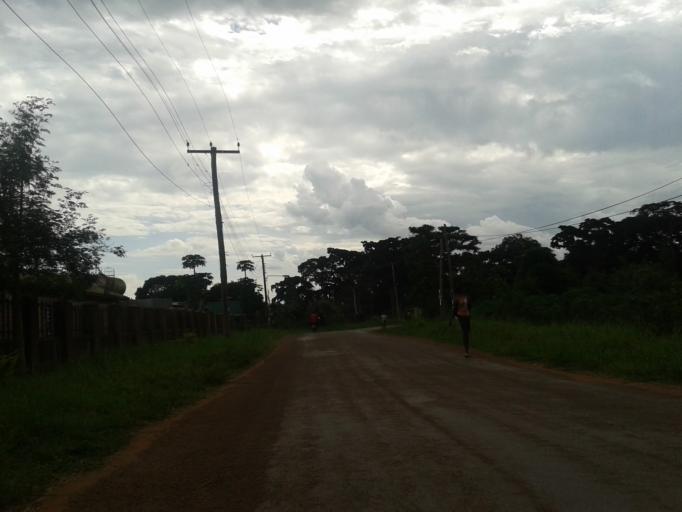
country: UG
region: Northern Region
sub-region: Gulu District
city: Gulu
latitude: 2.7791
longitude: 32.2991
